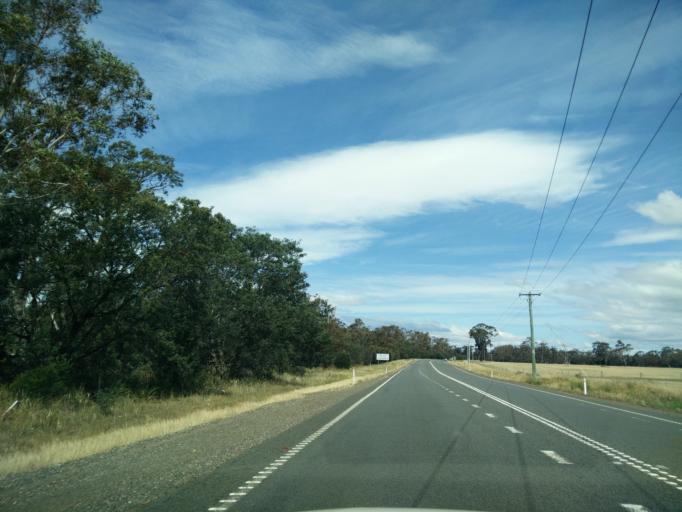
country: AU
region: Tasmania
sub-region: Northern Midlands
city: Evandale
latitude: -41.8088
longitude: 147.4095
